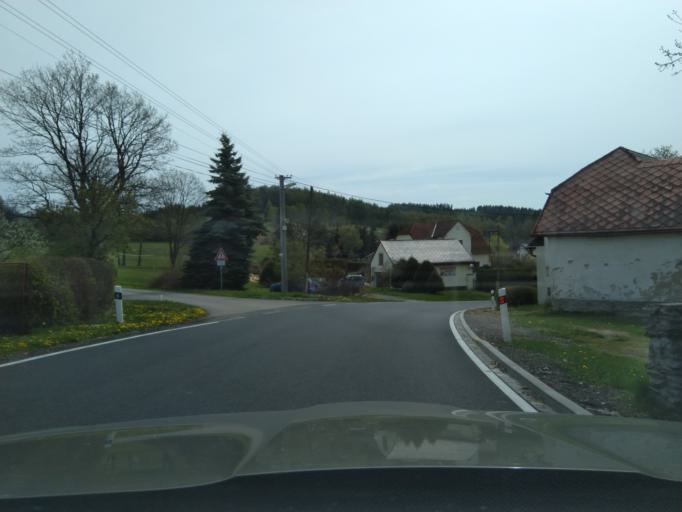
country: CZ
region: Jihocesky
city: Vacov
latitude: 49.1333
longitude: 13.7370
